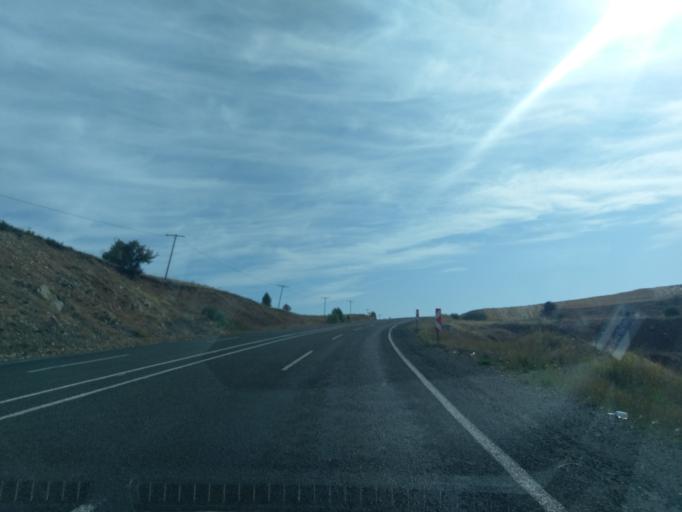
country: TR
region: Sivas
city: Zara
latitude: 39.8611
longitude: 37.8780
